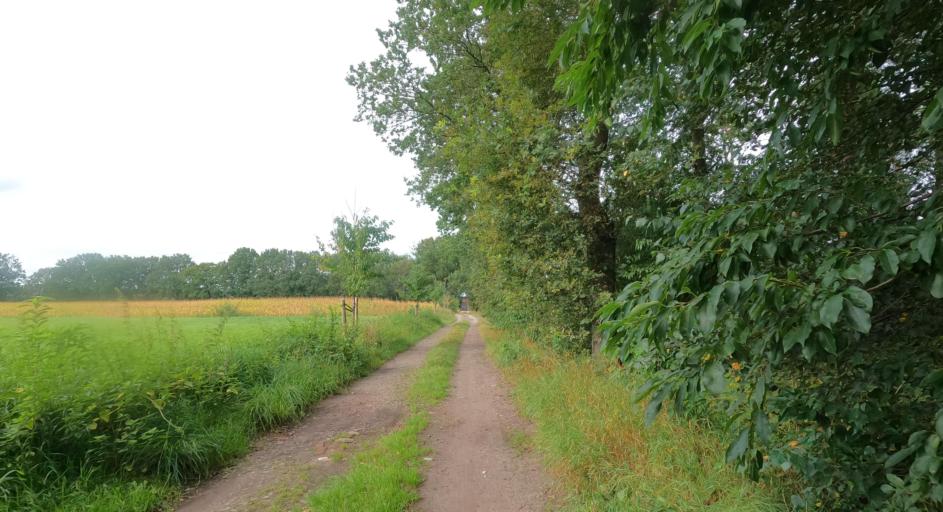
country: BE
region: Flanders
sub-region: Provincie Antwerpen
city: Essen
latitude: 51.4563
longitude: 4.5119
